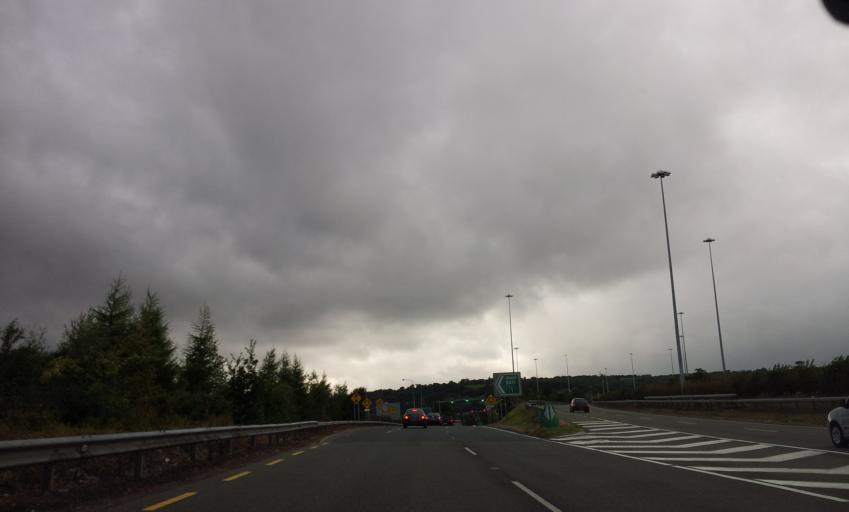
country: IE
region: Munster
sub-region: County Cork
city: Passage West
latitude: 51.9029
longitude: -8.3827
